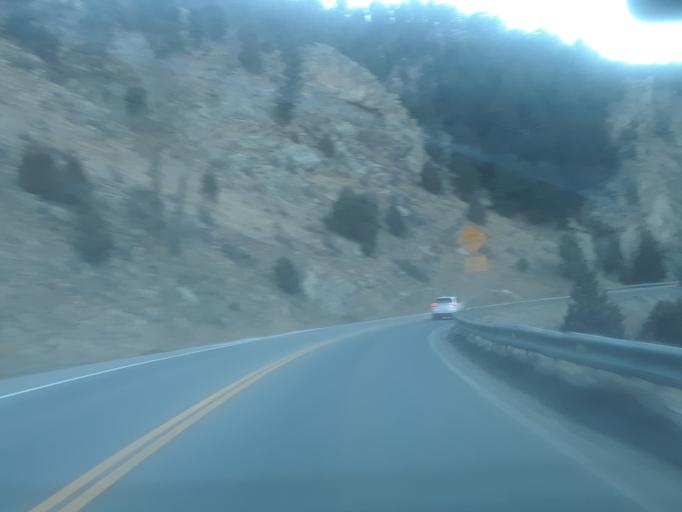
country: US
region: Colorado
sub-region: Clear Creek County
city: Idaho Springs
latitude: 39.7422
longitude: -105.4289
